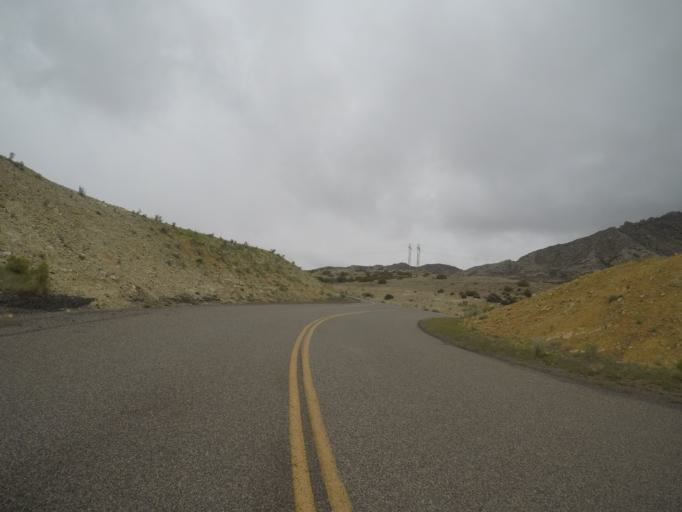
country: US
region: Wyoming
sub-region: Big Horn County
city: Lovell
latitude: 45.0261
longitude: -108.2653
